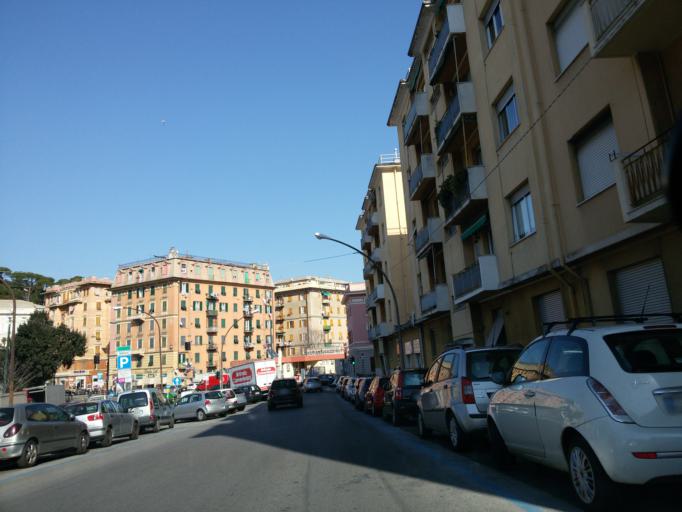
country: IT
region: Liguria
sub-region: Provincia di Genova
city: Genoa
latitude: 44.4063
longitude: 8.9600
